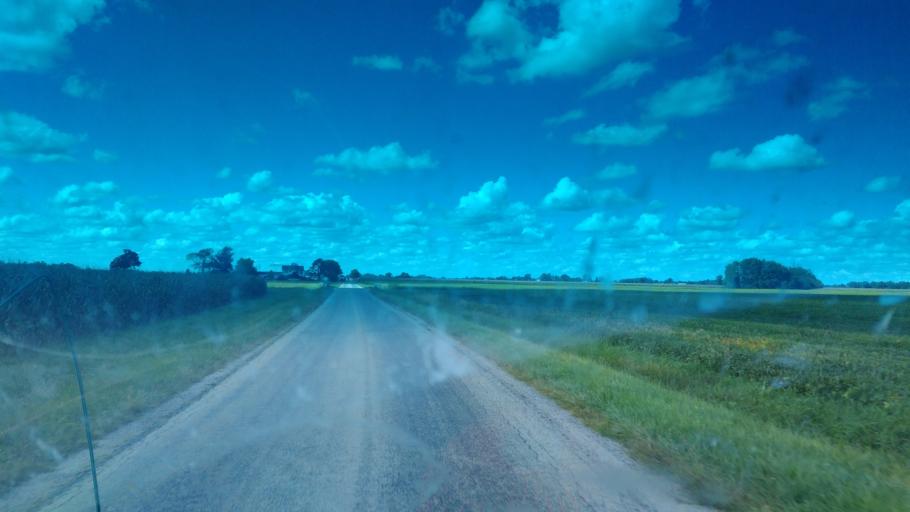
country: US
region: Ohio
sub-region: Madison County
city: Plain City
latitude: 40.0806
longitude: -83.3556
